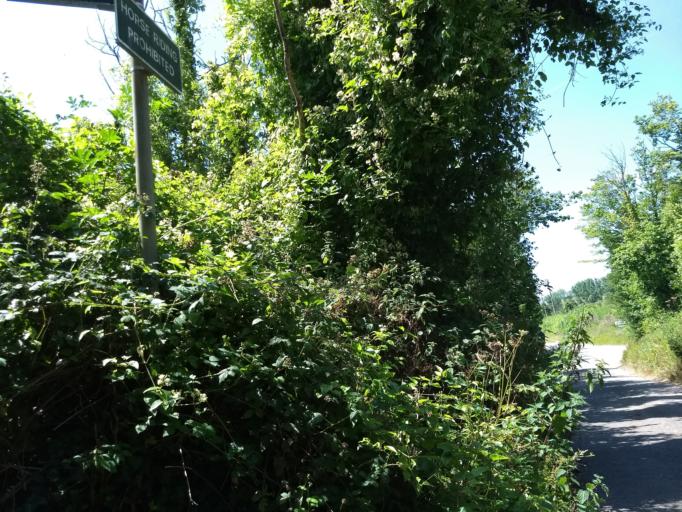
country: GB
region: England
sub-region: Isle of Wight
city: Brading
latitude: 50.6763
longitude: -1.1533
